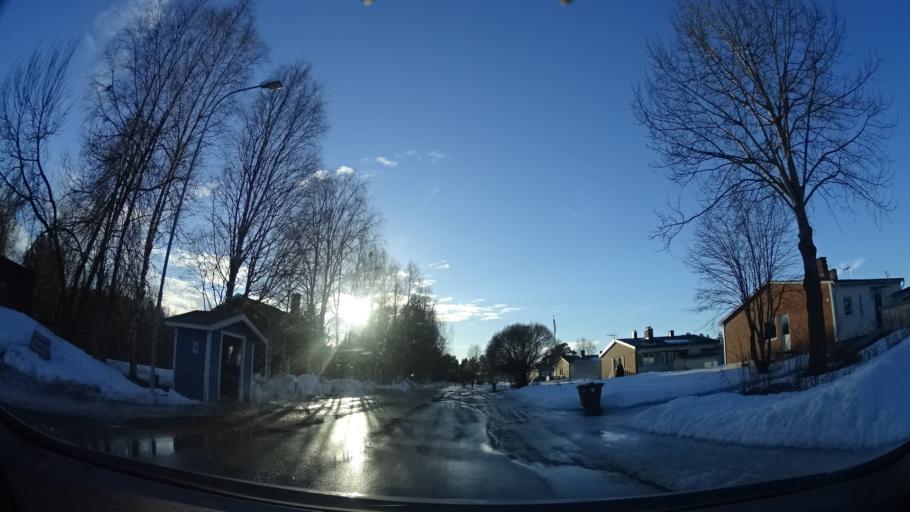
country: SE
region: Vaesterbotten
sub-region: Skelleftea Kommun
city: Byske
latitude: 64.9508
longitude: 21.2174
